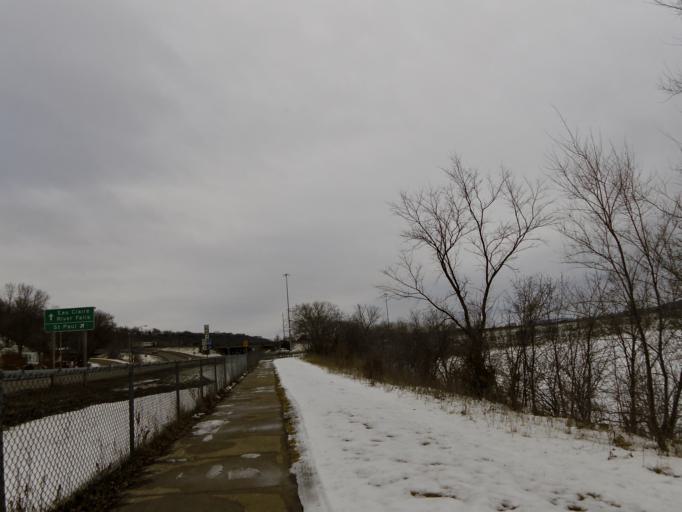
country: US
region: Wisconsin
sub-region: Saint Croix County
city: Hudson
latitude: 44.9650
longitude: -92.7545
